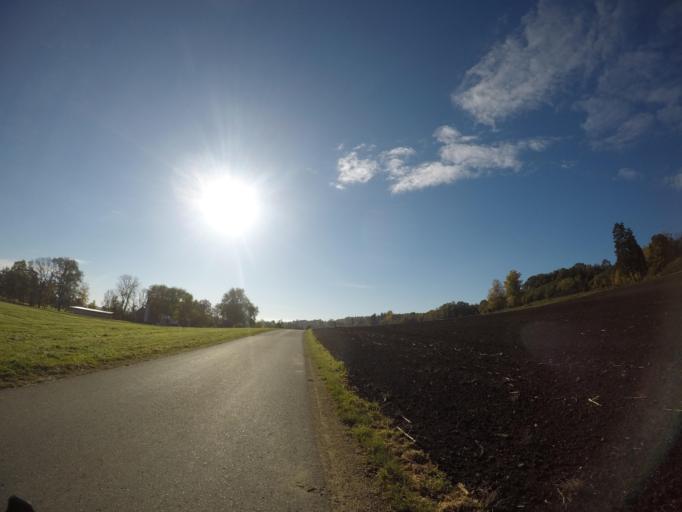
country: DE
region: Baden-Wuerttemberg
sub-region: Tuebingen Region
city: Saulgau
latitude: 48.0384
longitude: 9.4731
